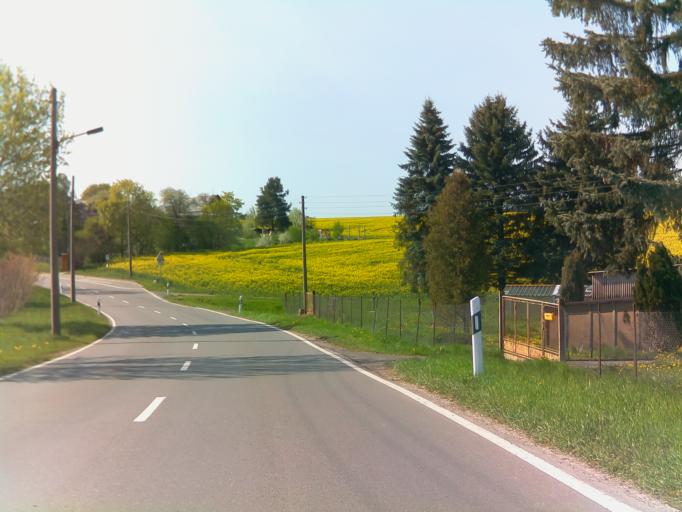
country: DE
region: Thuringia
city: Zeulenroda
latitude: 50.6271
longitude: 12.0291
